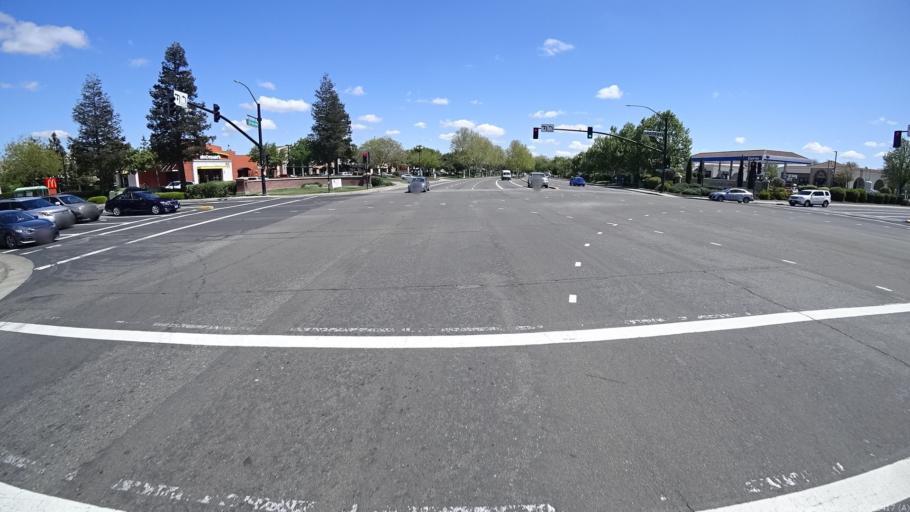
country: US
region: California
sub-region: Sacramento County
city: Laguna
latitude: 38.4086
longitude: -121.4774
